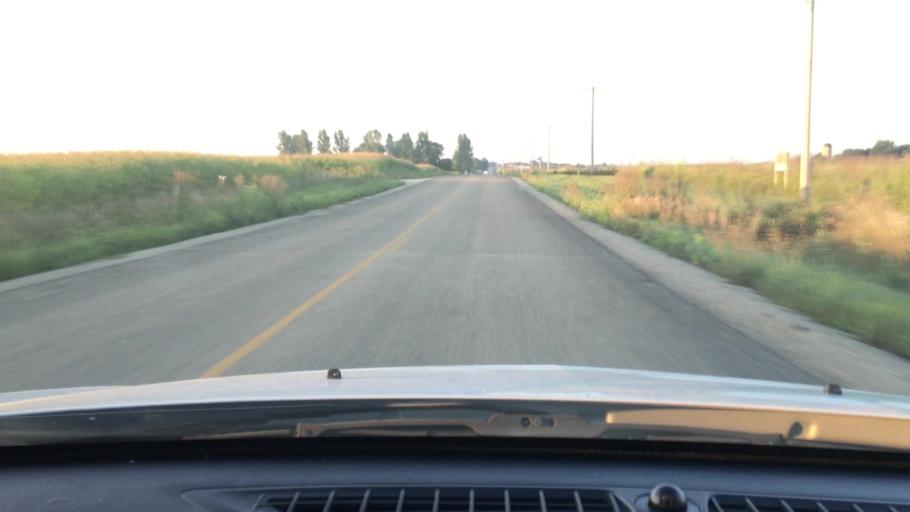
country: US
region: Illinois
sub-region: DeKalb County
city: Waterman
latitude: 41.8246
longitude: -88.7733
